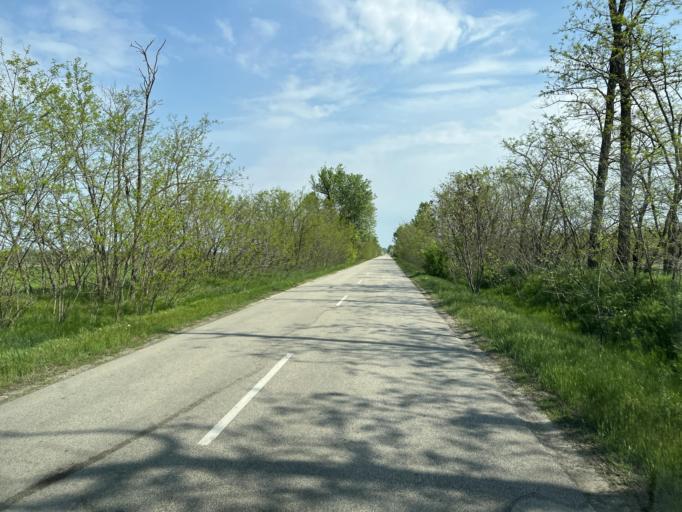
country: HU
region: Pest
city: Kocser
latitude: 47.0333
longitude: 19.9387
